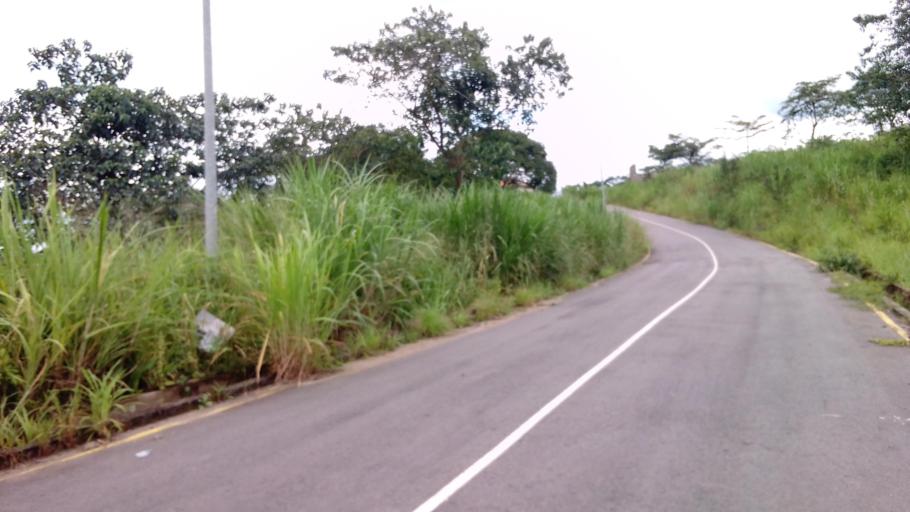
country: SL
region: Eastern Province
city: Koidu
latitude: 8.6594
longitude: -10.9870
